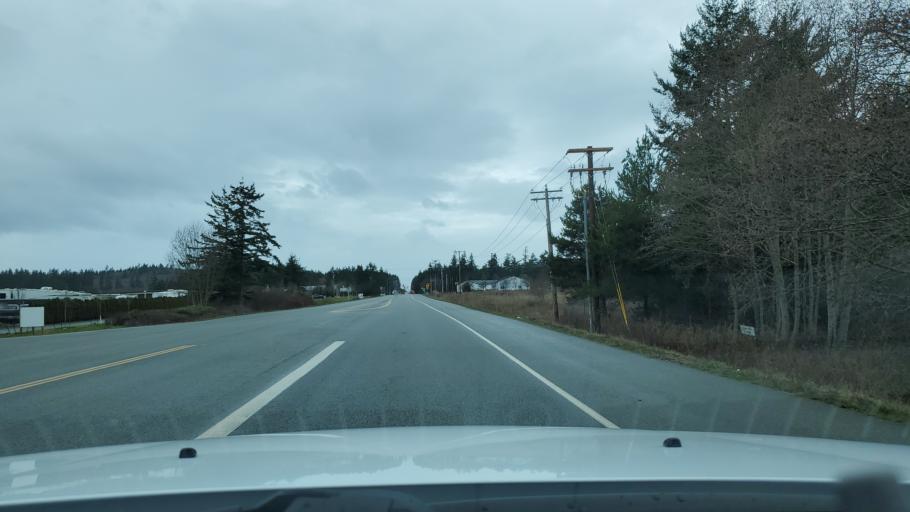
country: US
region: Washington
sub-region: Island County
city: Oak Harbor
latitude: 48.3259
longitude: -122.6434
